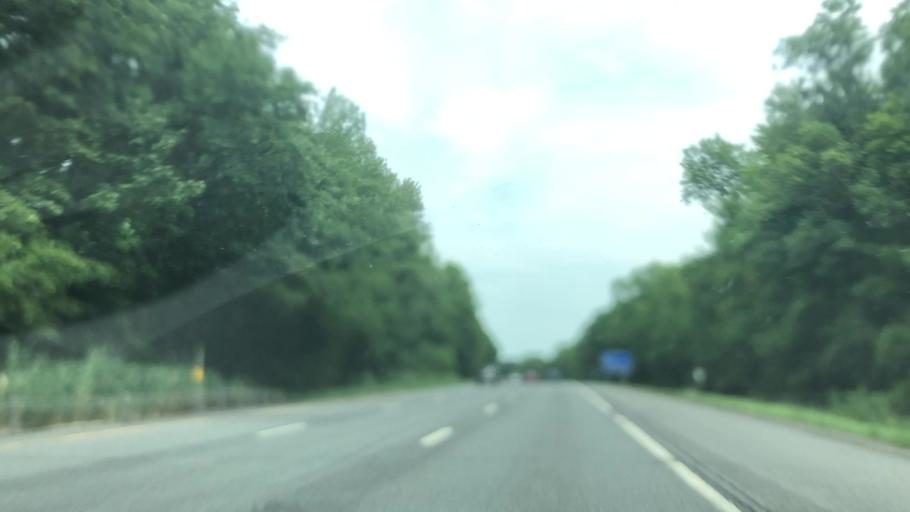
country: US
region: New York
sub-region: Saratoga County
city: Saratoga Springs
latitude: 43.0612
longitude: -73.7589
